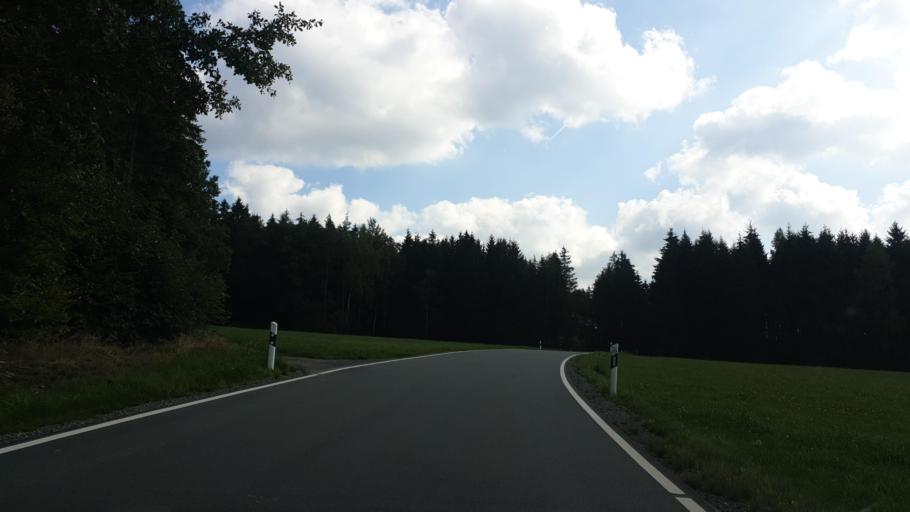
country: DE
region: Saxony
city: Rodewisch
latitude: 50.5119
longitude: 12.4412
